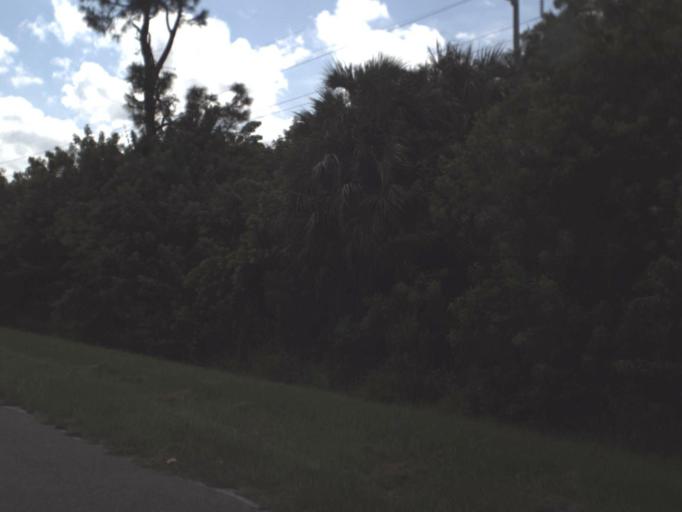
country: US
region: Florida
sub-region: Collier County
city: Immokalee
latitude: 26.3942
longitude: -81.3817
